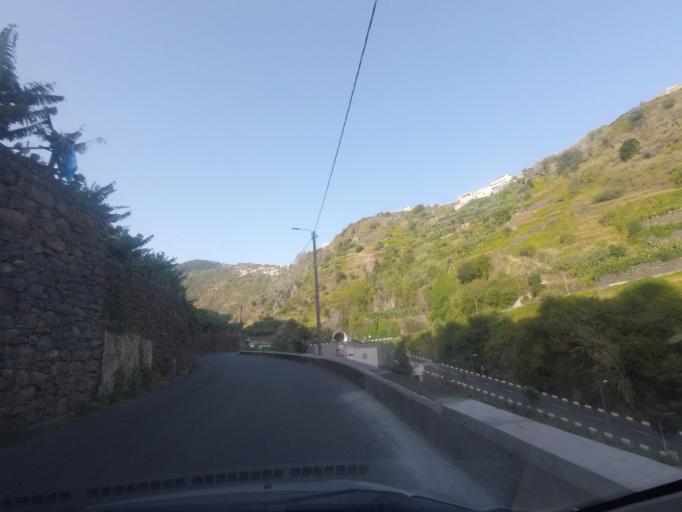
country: PT
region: Madeira
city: Ponta do Sol
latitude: 32.6850
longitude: -17.1005
